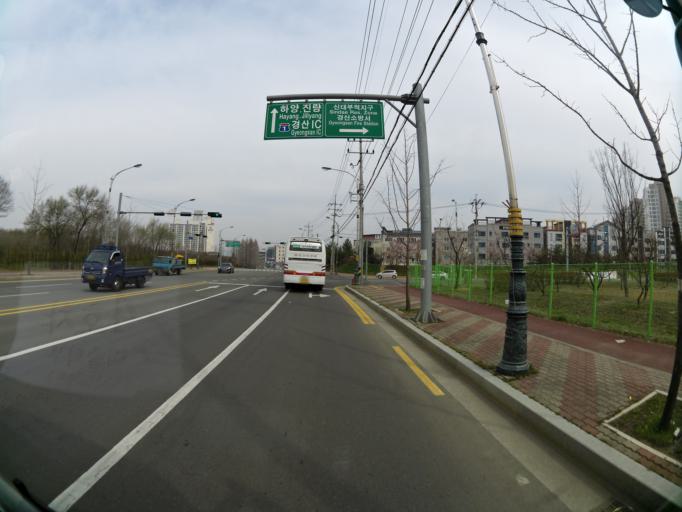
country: KR
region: Gyeongsangbuk-do
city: Gyeongsan-si
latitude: 35.8370
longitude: 128.7648
